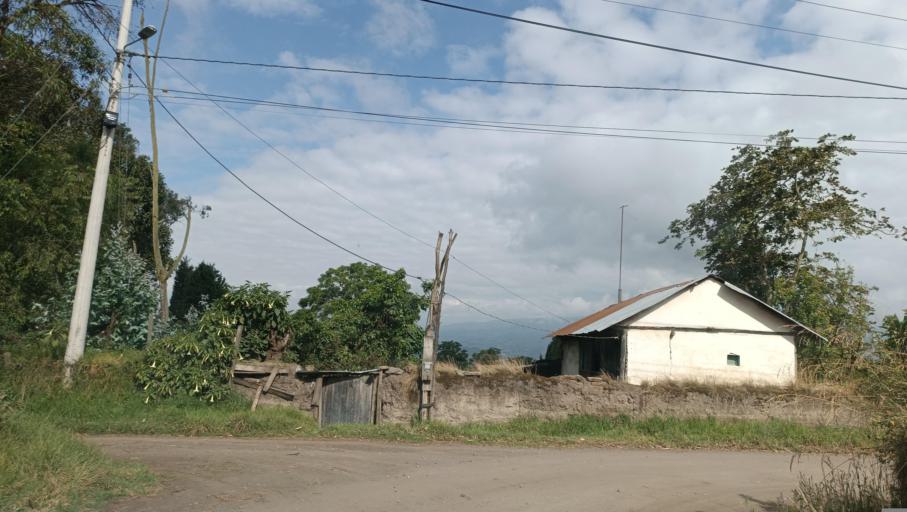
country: EC
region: Chimborazo
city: Guano
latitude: -1.6550
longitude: -78.5682
